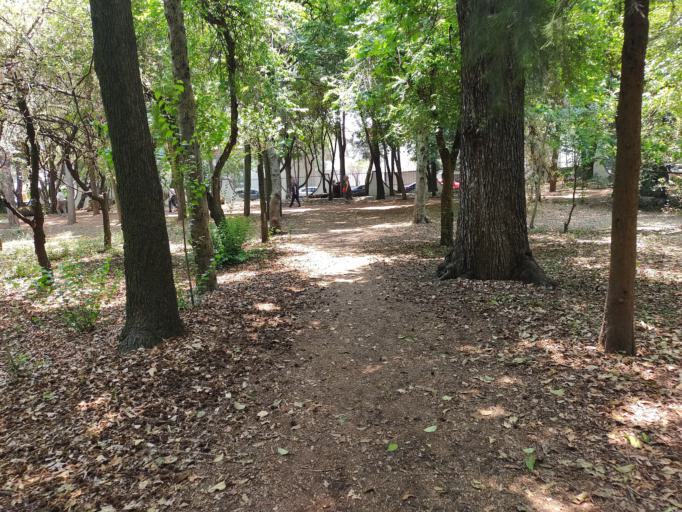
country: MX
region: Mexico City
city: Coyoacan
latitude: 19.3526
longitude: -99.1696
